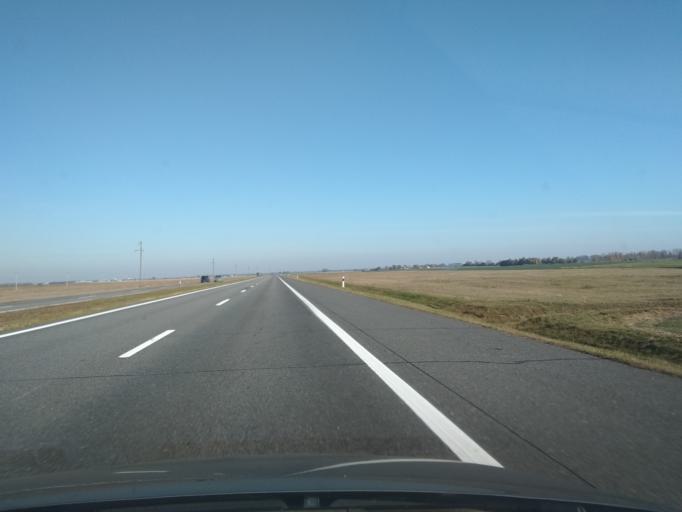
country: BY
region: Brest
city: Byaroza
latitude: 52.4657
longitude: 24.9277
